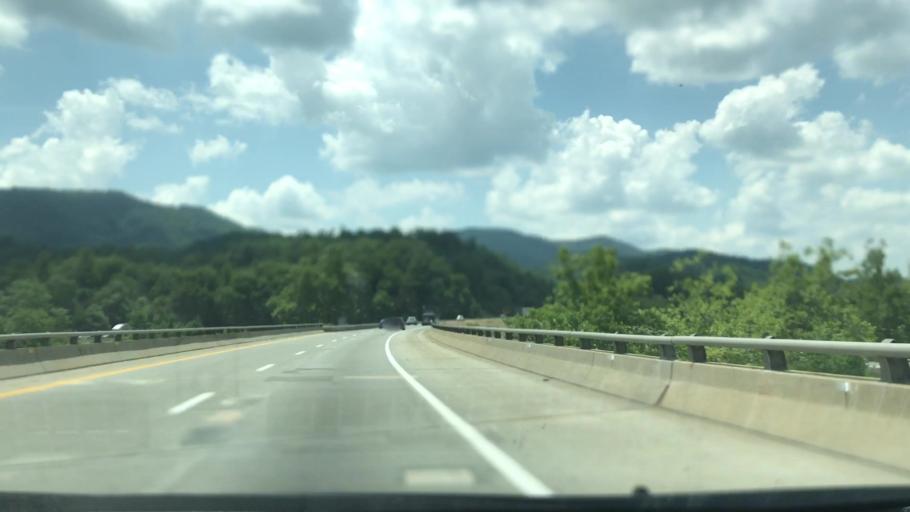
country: US
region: Virginia
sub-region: Bland County
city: Bland
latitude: 37.2158
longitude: -81.0927
